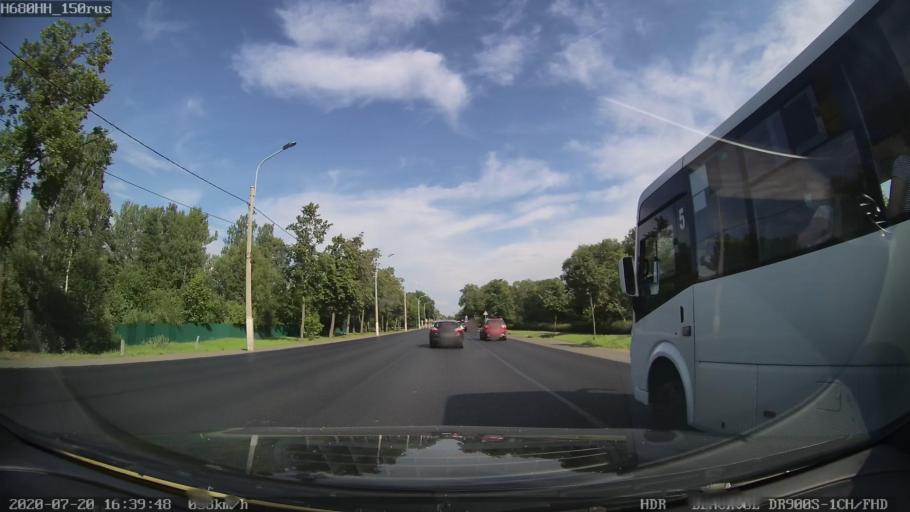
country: RU
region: Leningrad
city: Ol'gino
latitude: 59.8734
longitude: 29.9549
